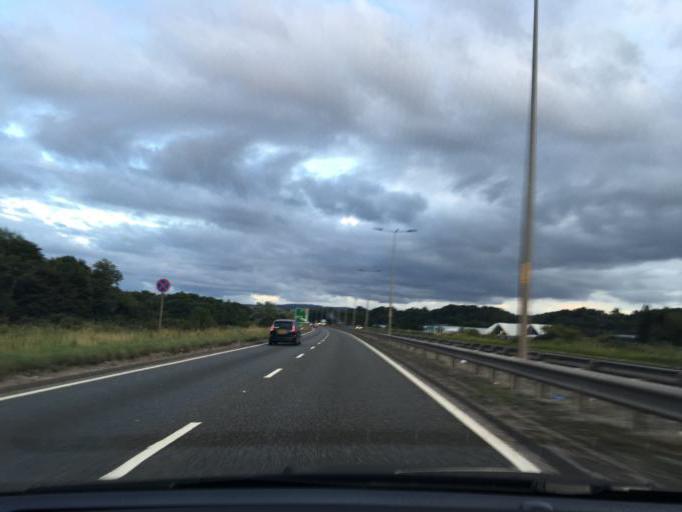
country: GB
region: Scotland
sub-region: Highland
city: Inverness
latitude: 57.4872
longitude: -4.2072
